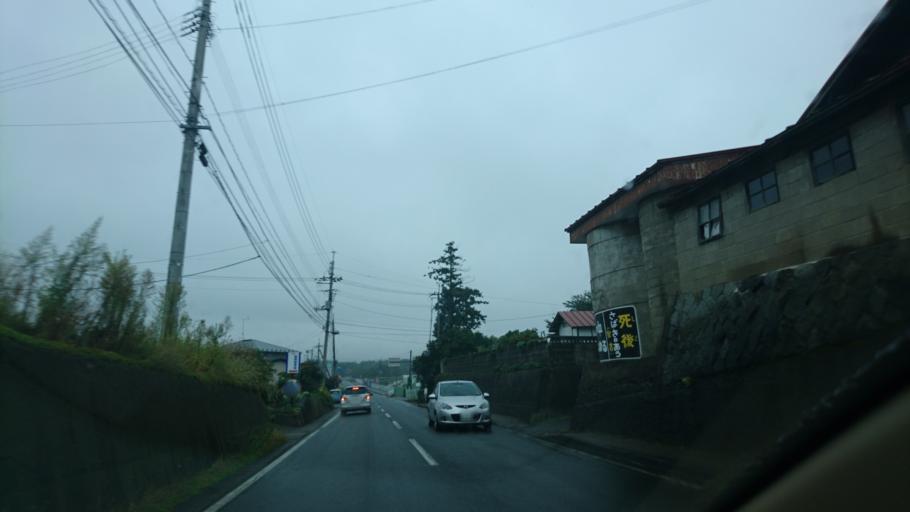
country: JP
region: Iwate
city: Mizusawa
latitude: 39.1355
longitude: 141.1661
